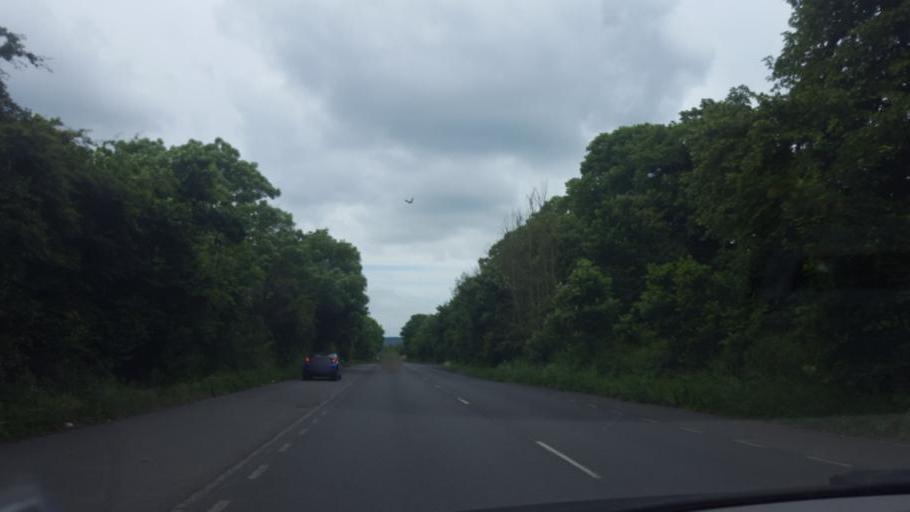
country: GB
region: England
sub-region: Royal Borough of Windsor and Maidenhead
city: Hurley
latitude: 51.5392
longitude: -0.8346
